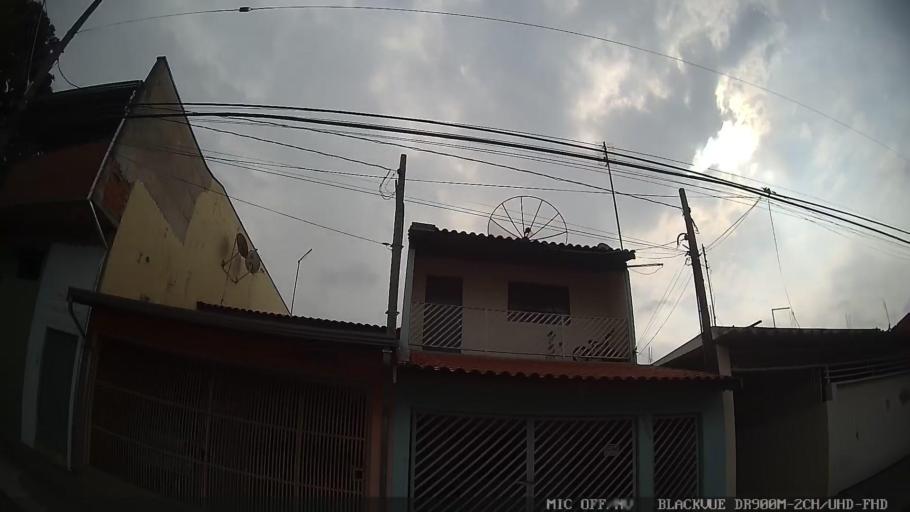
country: BR
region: Sao Paulo
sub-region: Indaiatuba
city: Indaiatuba
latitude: -23.1138
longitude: -47.2383
